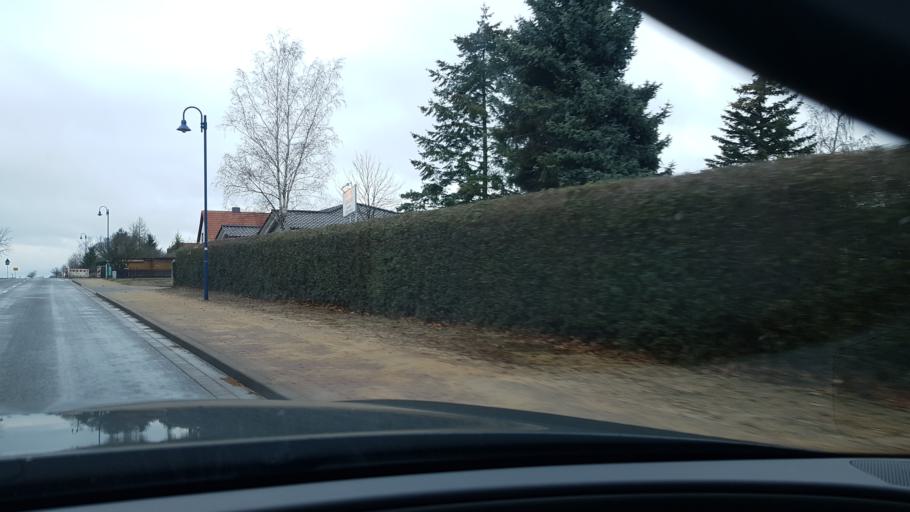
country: DE
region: Saxony-Anhalt
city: Weferlingen
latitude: 52.4040
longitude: 11.1069
